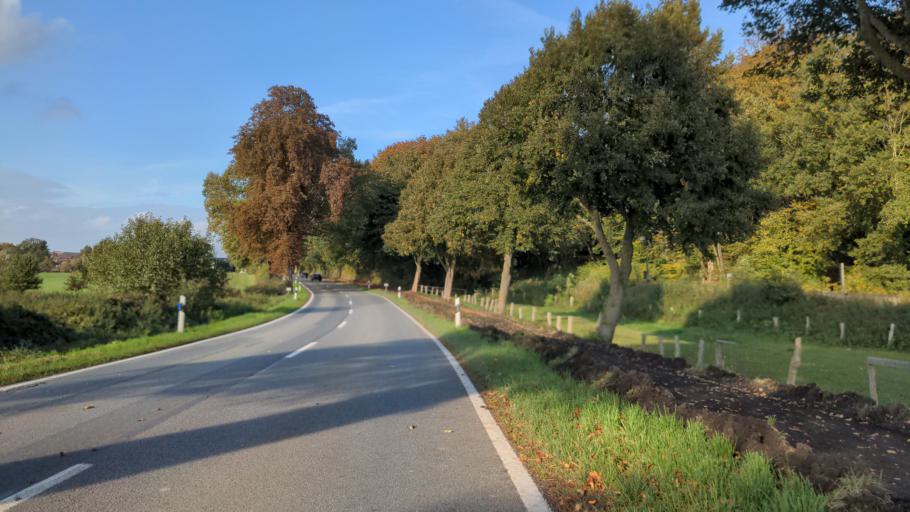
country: DE
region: Schleswig-Holstein
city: Lensahn
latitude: 54.2321
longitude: 10.8868
